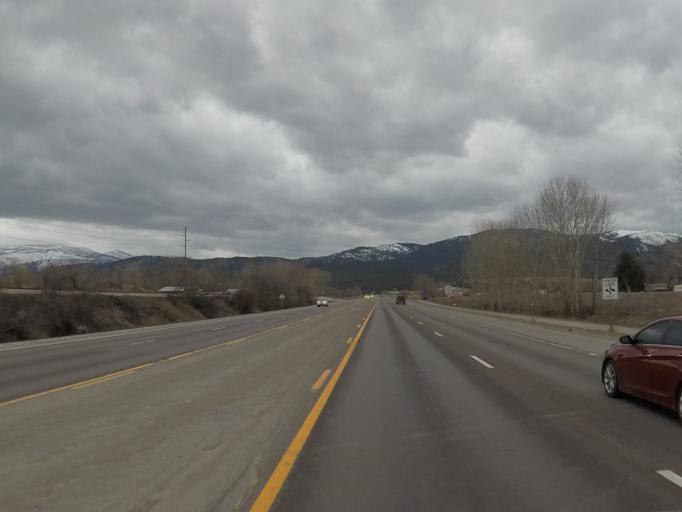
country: US
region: Montana
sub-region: Missoula County
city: Orchard Homes
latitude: 46.8306
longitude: -114.0573
